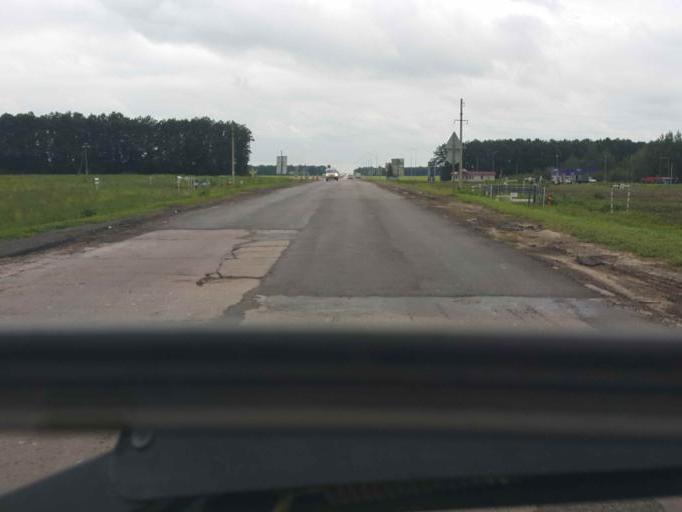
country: RU
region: Tambov
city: Zavoronezhskoye
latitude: 52.8905
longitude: 40.6986
